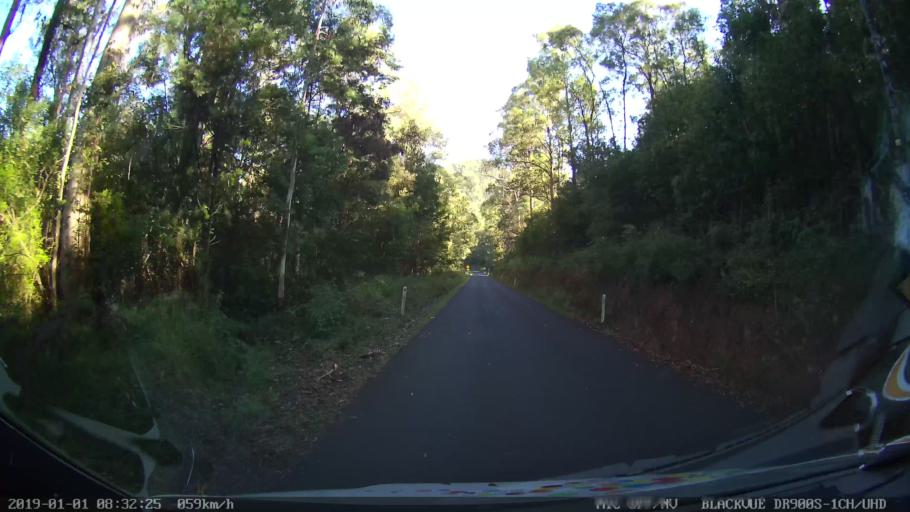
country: AU
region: New South Wales
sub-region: Snowy River
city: Jindabyne
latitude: -36.3621
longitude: 148.2060
